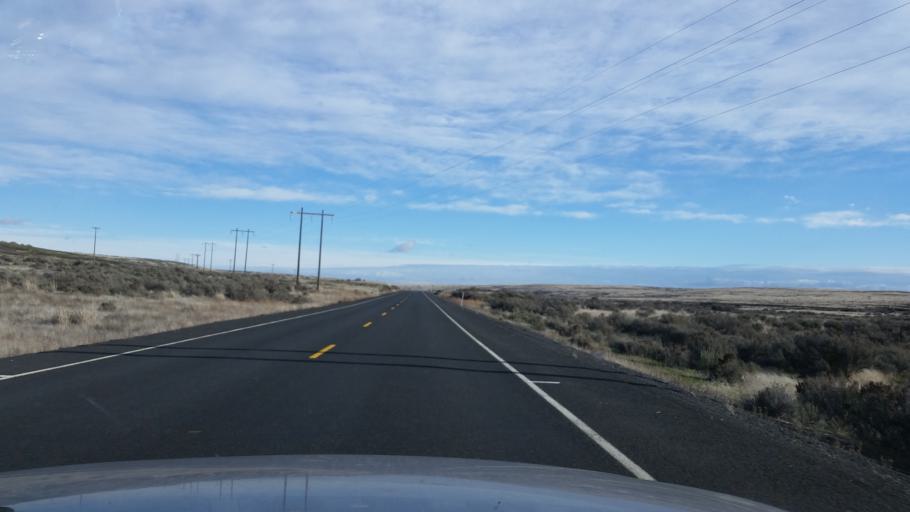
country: US
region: Washington
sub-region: Adams County
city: Ritzville
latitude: 47.3477
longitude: -118.5923
